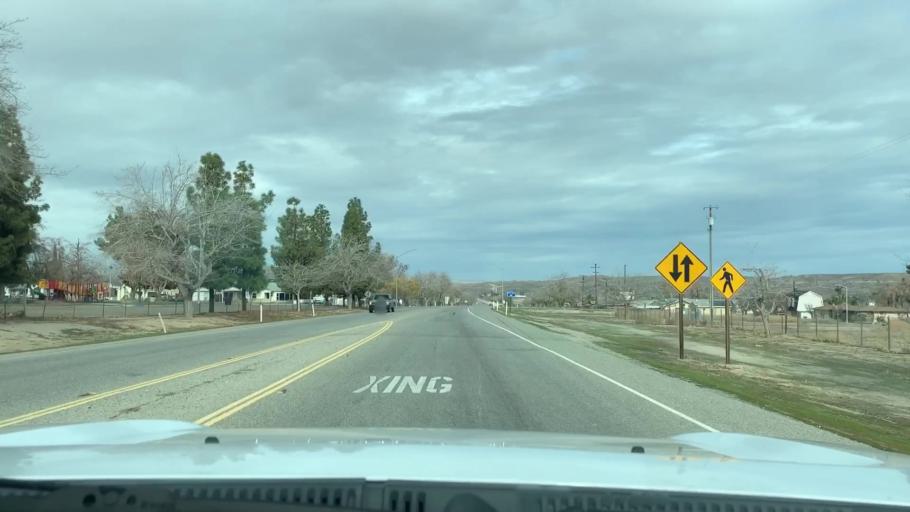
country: US
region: California
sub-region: Kern County
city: Taft
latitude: 35.1395
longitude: -119.4472
